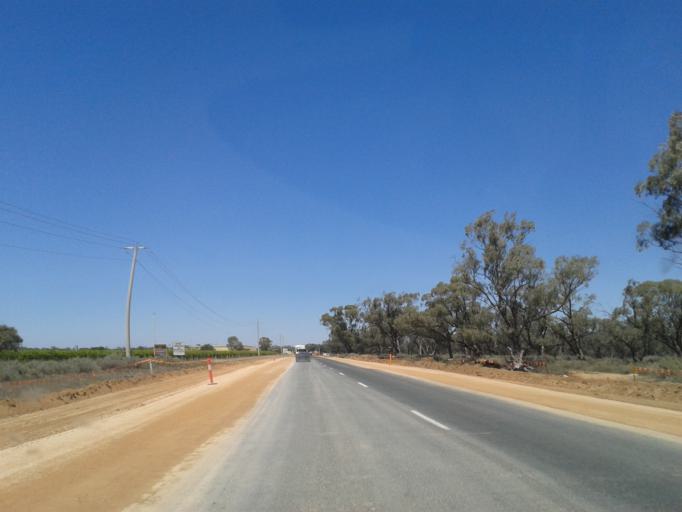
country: AU
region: New South Wales
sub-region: Wentworth
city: Gol Gol
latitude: -34.5657
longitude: 142.7280
